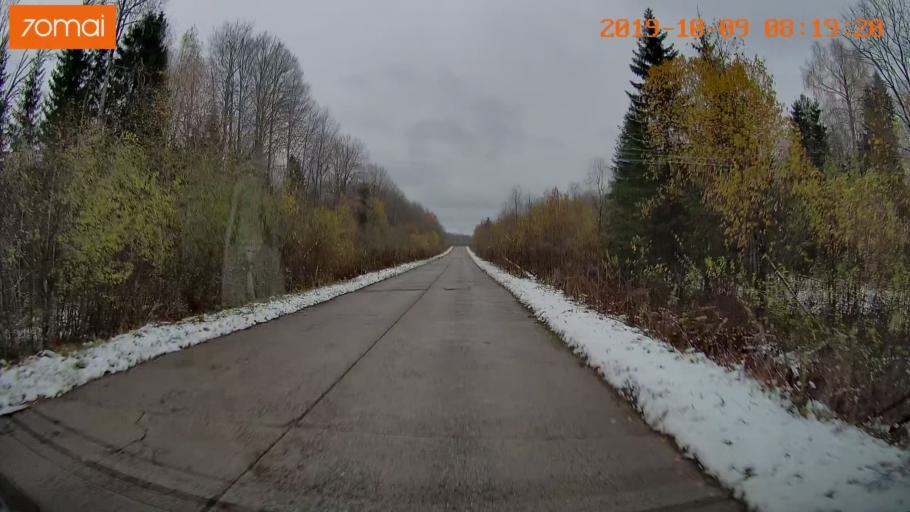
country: RU
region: Vologda
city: Gryazovets
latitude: 58.7418
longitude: 40.2400
